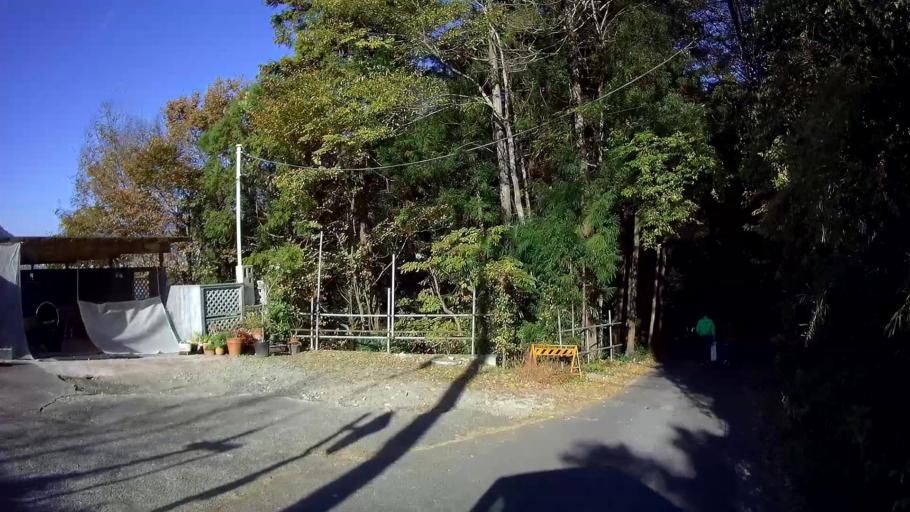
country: JP
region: Yamanashi
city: Uenohara
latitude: 35.6165
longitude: 139.1254
